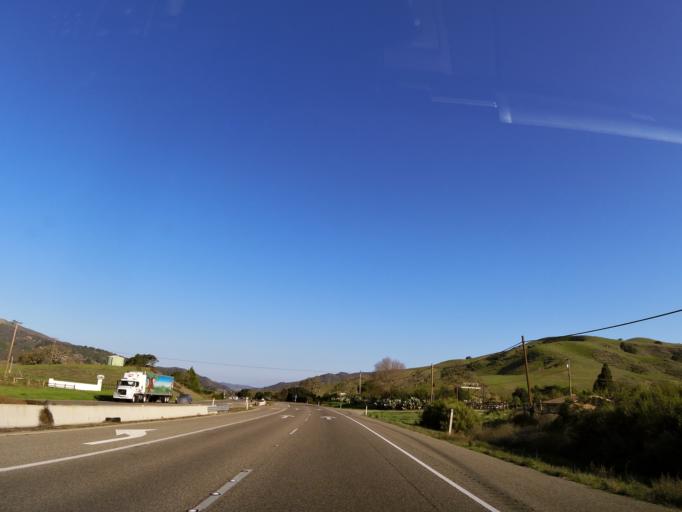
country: US
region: California
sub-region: Santa Barbara County
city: Buellton
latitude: 34.5505
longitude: -120.1914
